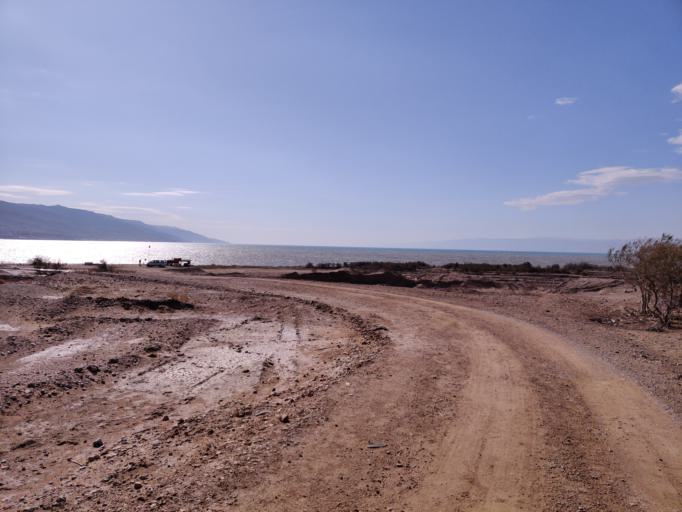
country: PS
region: West Bank
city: Jericho
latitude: 31.7625
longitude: 35.5746
